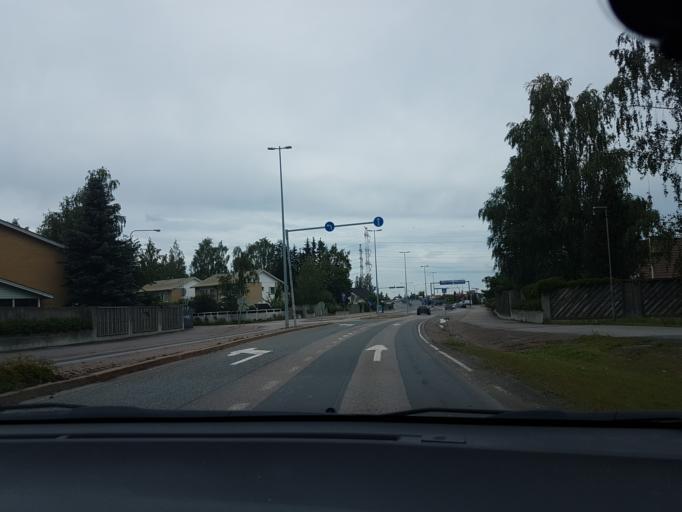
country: FI
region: Uusimaa
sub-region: Helsinki
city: Vantaa
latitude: 60.2795
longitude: 25.0286
